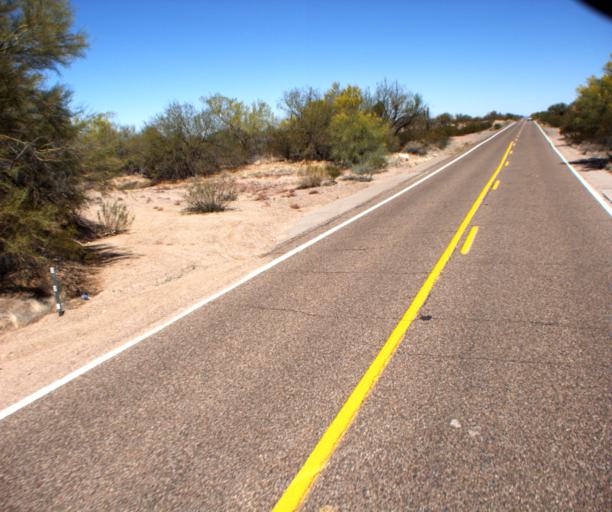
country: US
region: Arizona
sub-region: Pima County
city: Ajo
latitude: 32.1496
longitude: -112.7654
